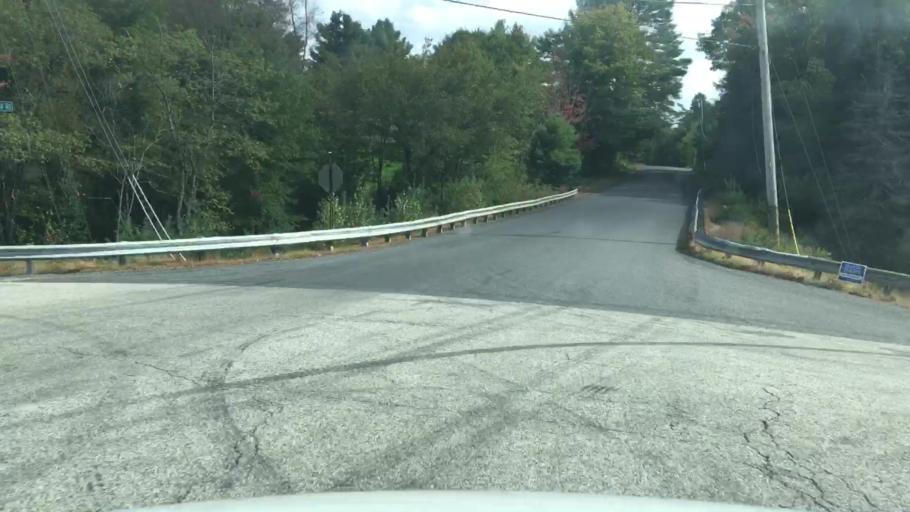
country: US
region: Maine
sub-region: Androscoggin County
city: Lisbon Falls
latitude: 43.9834
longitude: -70.1010
